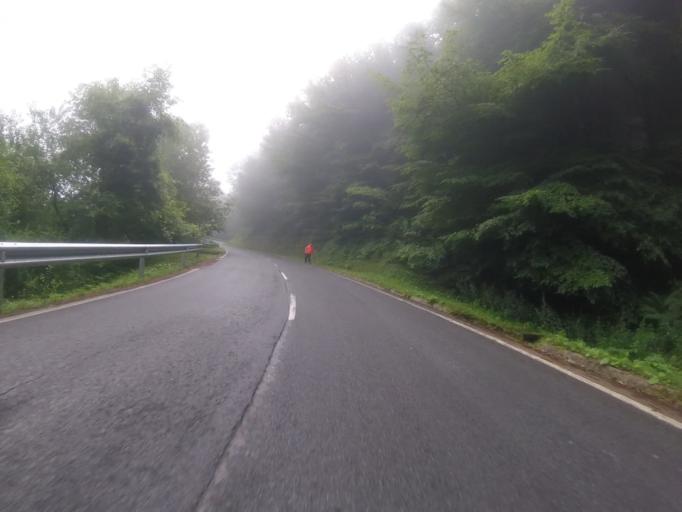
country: ES
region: Navarre
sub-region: Provincia de Navarra
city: Leitza
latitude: 43.0853
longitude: -1.8689
